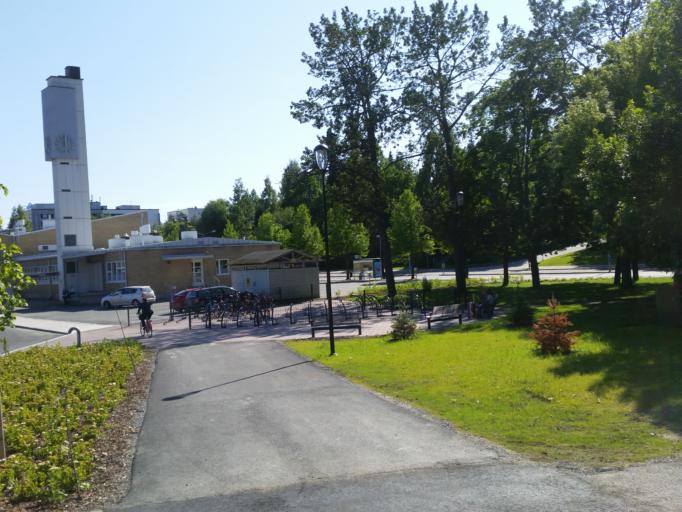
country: FI
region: Northern Savo
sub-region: Kuopio
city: Kuopio
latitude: 62.8990
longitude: 27.6793
